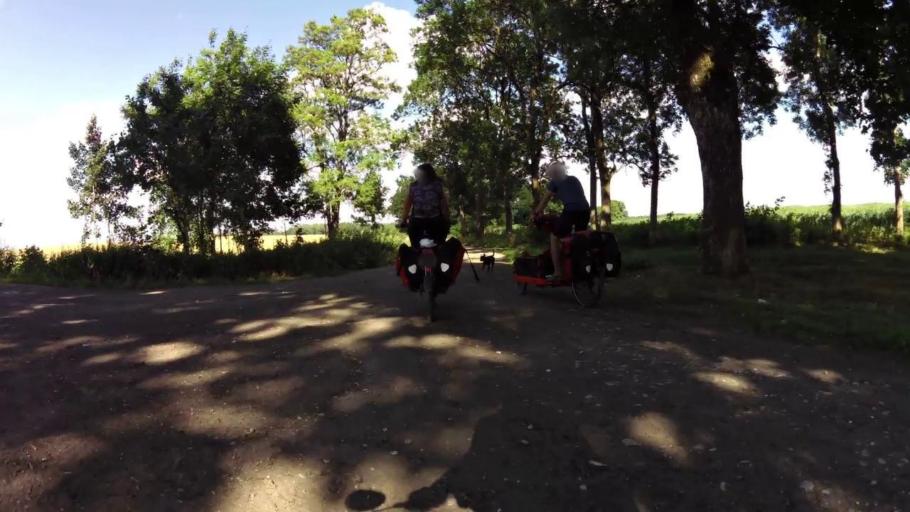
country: PL
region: West Pomeranian Voivodeship
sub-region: Powiat lobeski
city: Lobez
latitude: 53.6725
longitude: 15.6901
